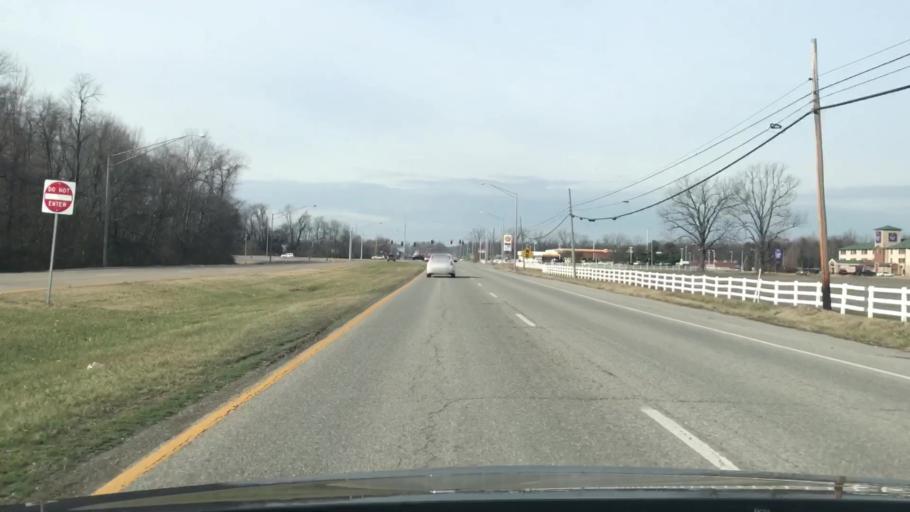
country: US
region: Kentucky
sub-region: Daviess County
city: Owensboro
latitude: 37.7743
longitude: -87.1625
